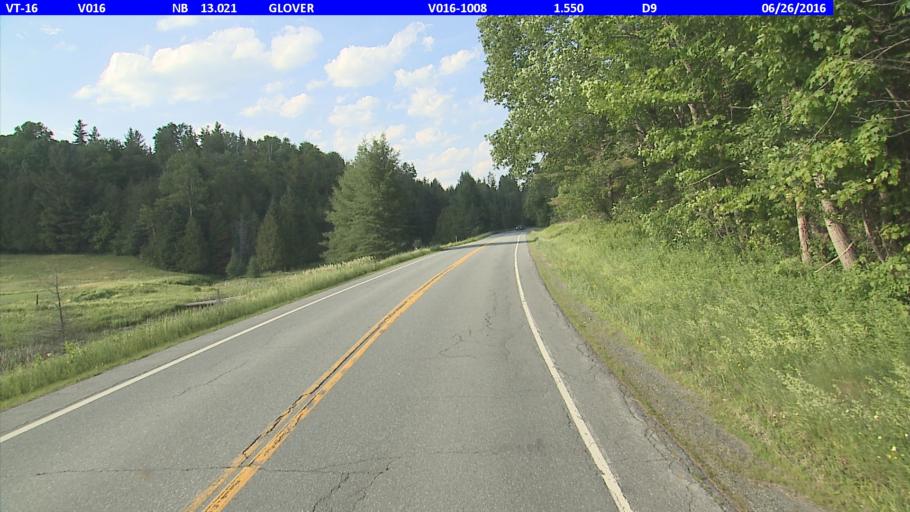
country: US
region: Vermont
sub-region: Caledonia County
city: Hardwick
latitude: 44.6473
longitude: -72.2018
